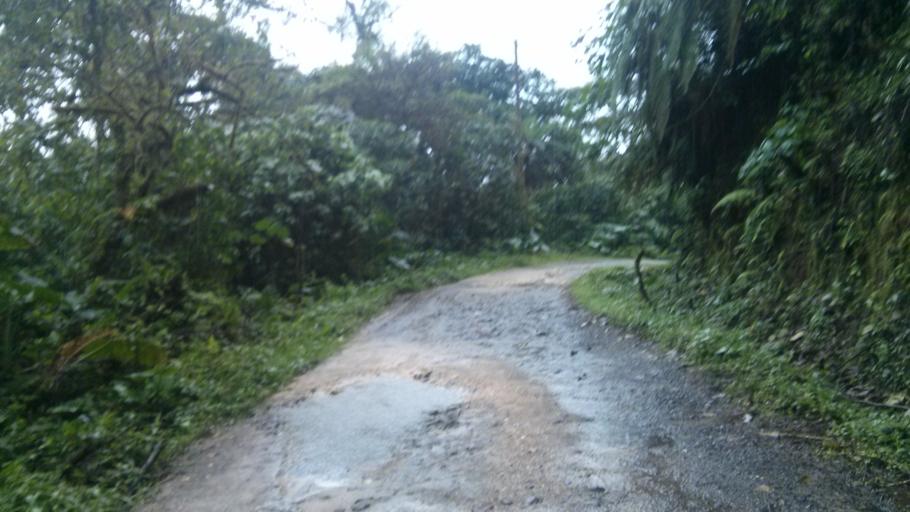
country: CR
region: San Jose
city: Ipis
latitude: 10.0296
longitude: -83.9419
